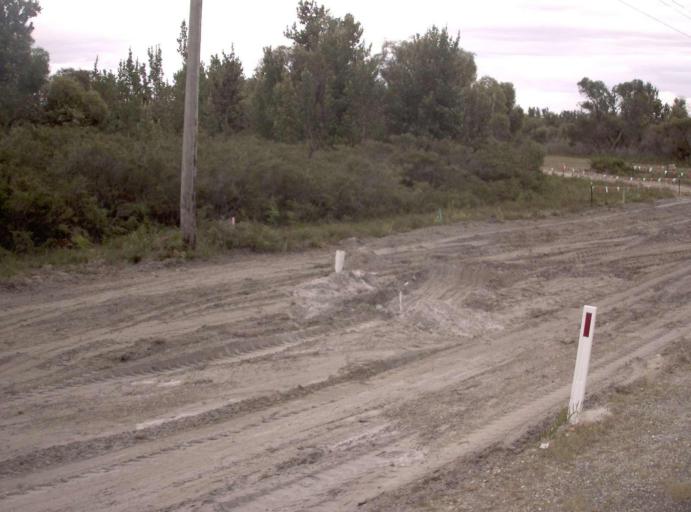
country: AU
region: Victoria
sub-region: East Gippsland
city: Bairnsdale
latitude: -38.0818
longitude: 147.5317
